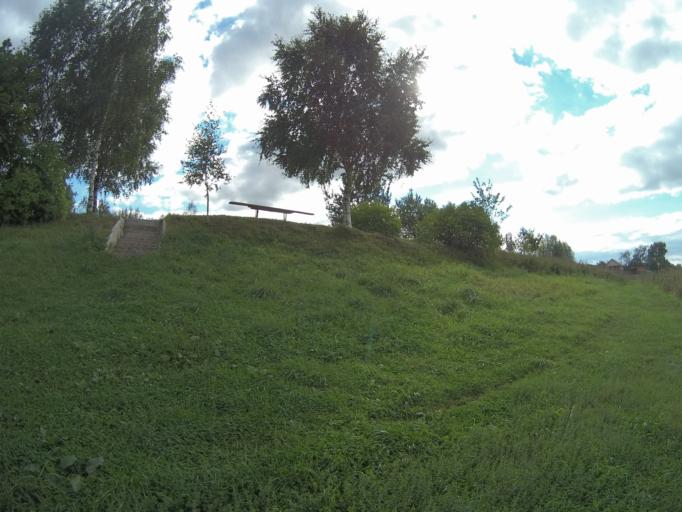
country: RU
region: Vladimir
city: Orgtrud
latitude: 56.3206
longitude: 40.6514
